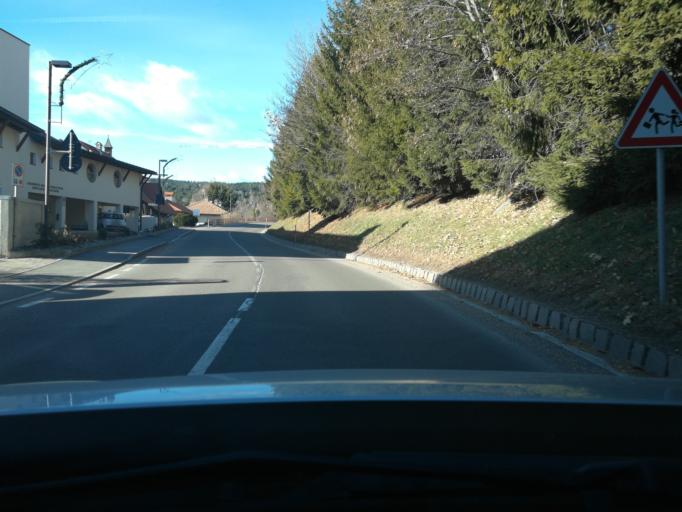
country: IT
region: Trentino-Alto Adige
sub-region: Bolzano
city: Collalbo
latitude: 46.5381
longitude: 11.4601
